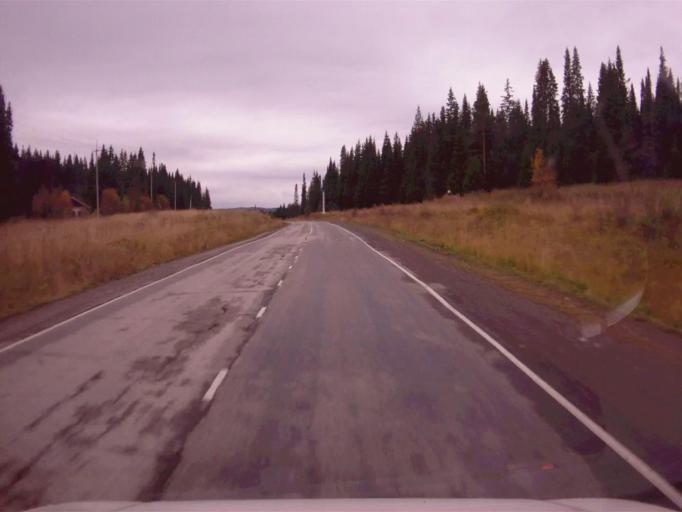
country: RU
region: Chelyabinsk
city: Nyazepetrovsk
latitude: 56.0662
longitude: 59.6357
